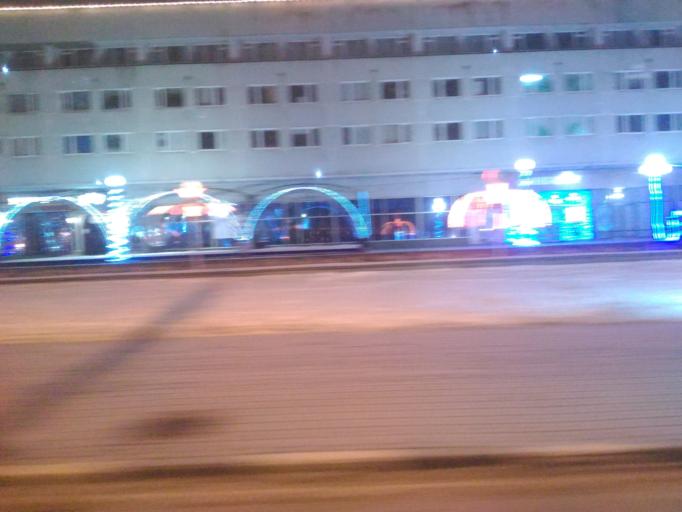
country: RU
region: Ulyanovsk
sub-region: Ulyanovskiy Rayon
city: Ulyanovsk
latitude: 54.3203
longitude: 48.4044
